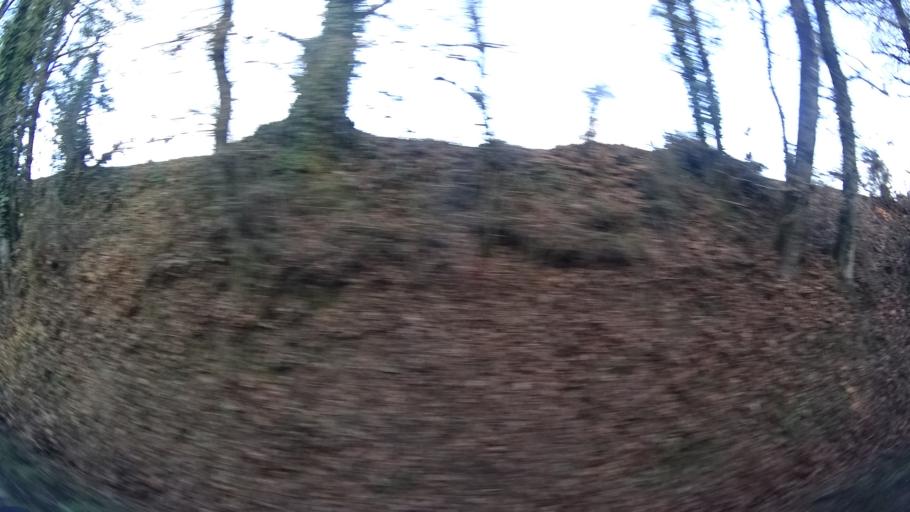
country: FR
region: Pays de la Loire
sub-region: Departement de la Loire-Atlantique
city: Fegreac
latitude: 47.6018
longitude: -2.0223
